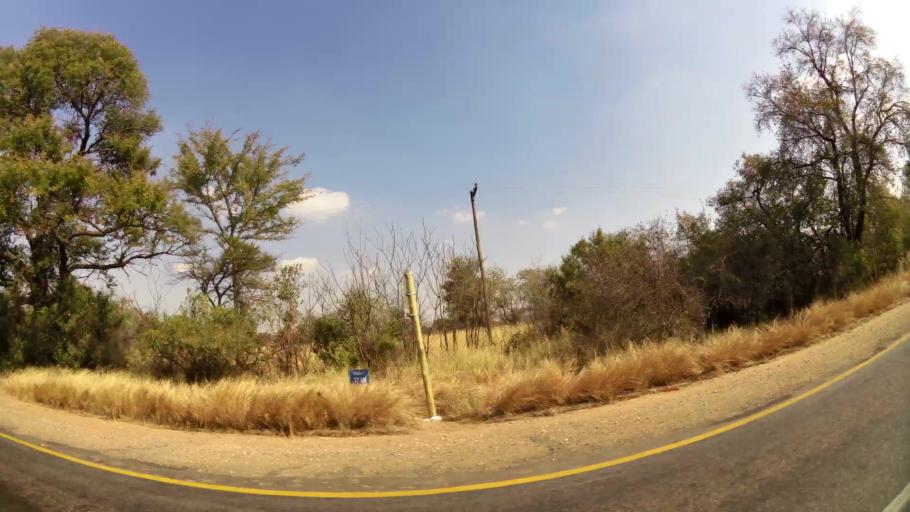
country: ZA
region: North-West
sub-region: Bojanala Platinum District Municipality
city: Rustenburg
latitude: -25.5195
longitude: 27.1039
